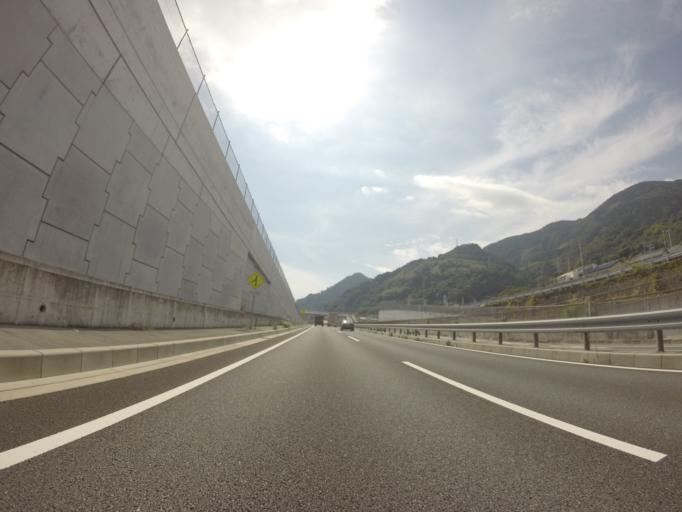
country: JP
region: Shizuoka
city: Fujinomiya
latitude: 35.0934
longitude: 138.5512
